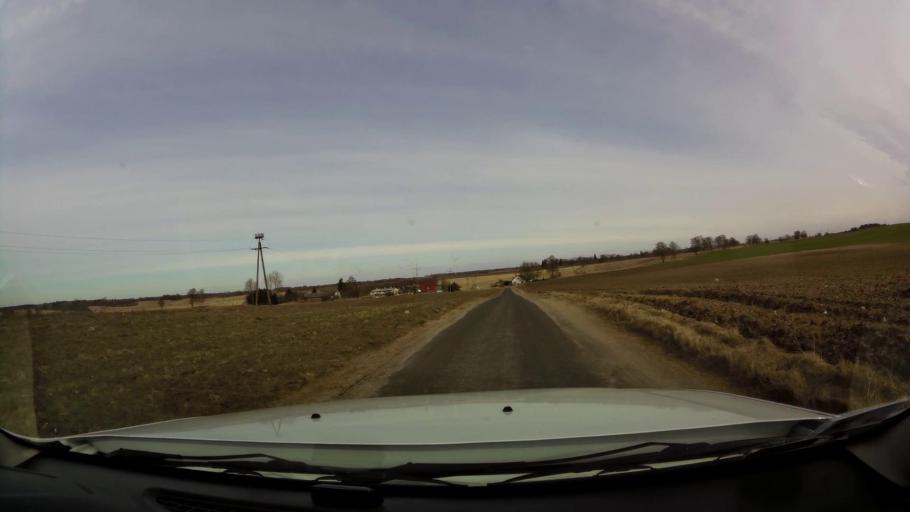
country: PL
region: West Pomeranian Voivodeship
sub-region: Powiat drawski
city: Drawsko Pomorskie
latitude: 53.5268
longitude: 15.7604
